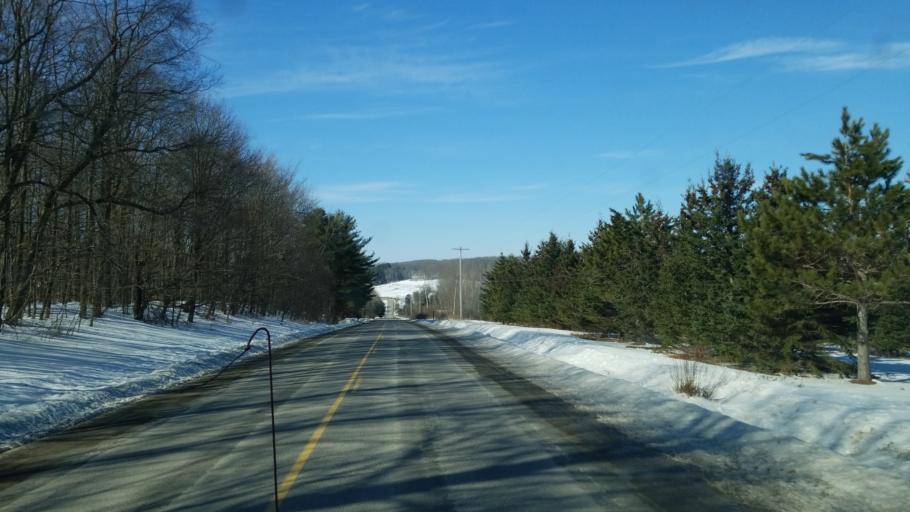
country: US
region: New York
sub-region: Allegany County
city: Andover
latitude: 42.0880
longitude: -77.7729
